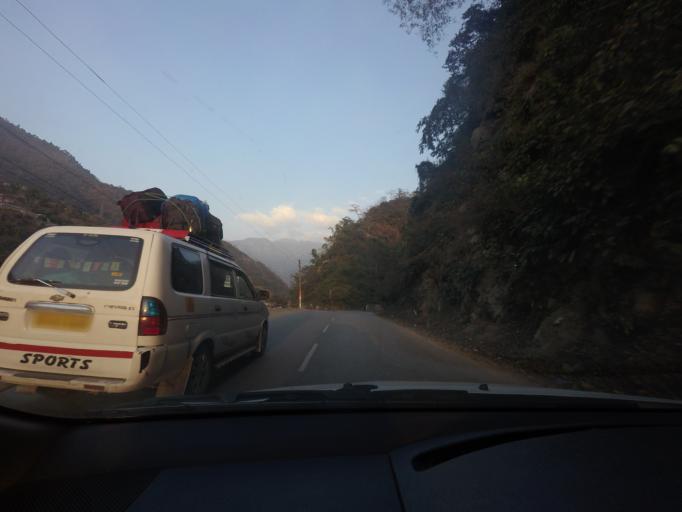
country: IN
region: Himachal Pradesh
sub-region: Mandi
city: Mandi
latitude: 31.7071
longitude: 76.9811
